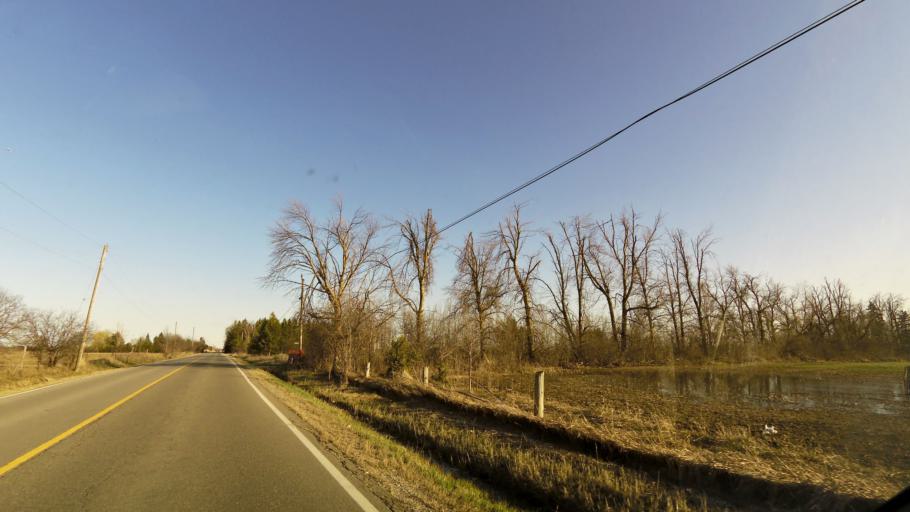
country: CA
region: Ontario
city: Brampton
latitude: 43.8293
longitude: -79.6931
